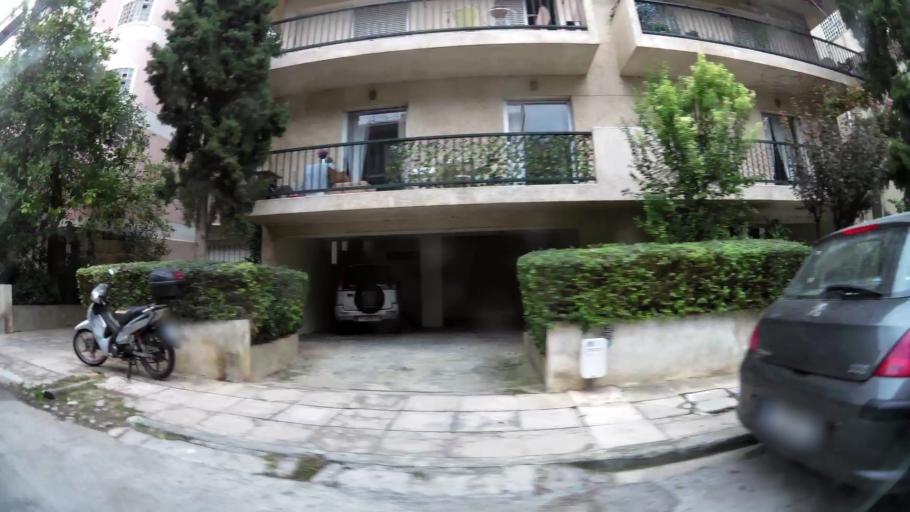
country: GR
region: Attica
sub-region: Nomarchia Athinas
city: Palaio Faliro
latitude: 37.9192
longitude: 23.7040
